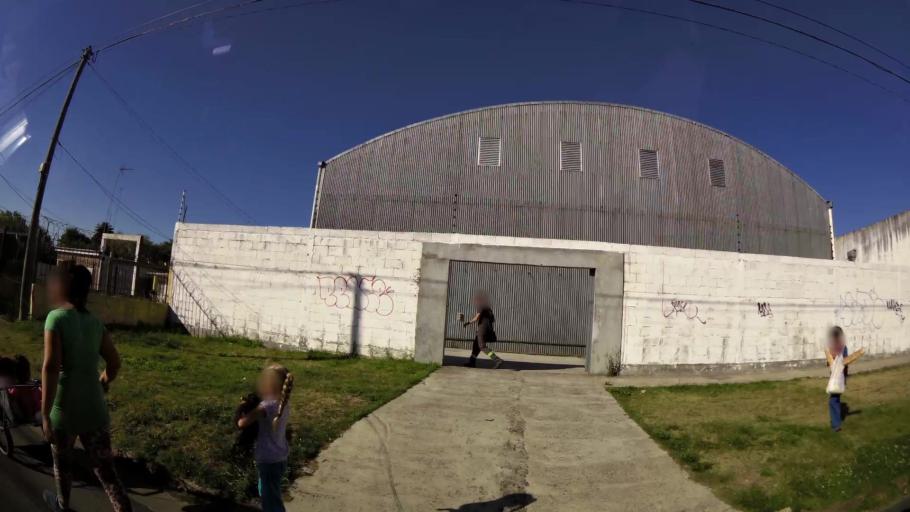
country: UY
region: Canelones
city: La Paz
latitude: -34.8182
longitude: -56.2226
